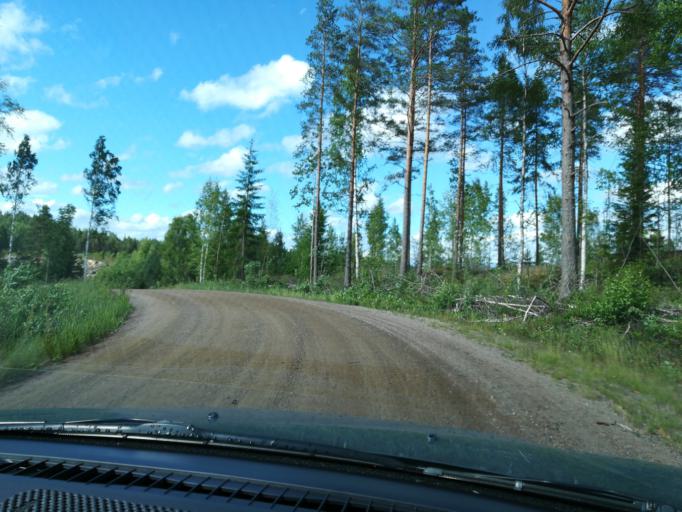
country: FI
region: South Karelia
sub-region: Lappeenranta
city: Savitaipale
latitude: 61.3001
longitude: 27.6400
